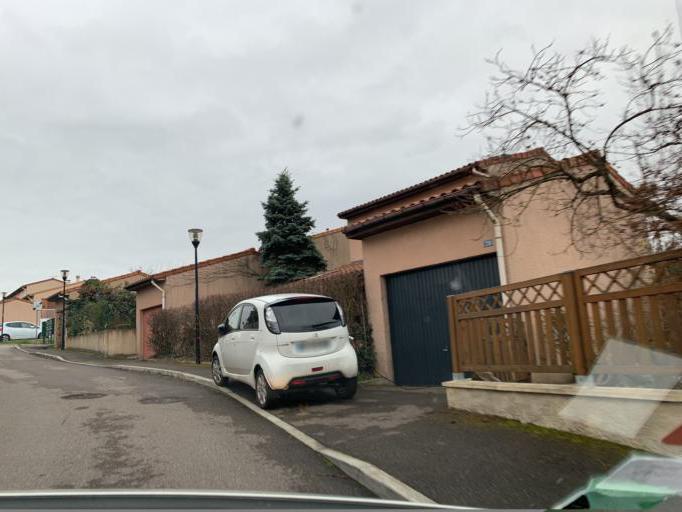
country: FR
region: Rhone-Alpes
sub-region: Departement du Rhone
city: Rillieux-la-Pape
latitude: 45.8347
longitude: 4.9066
